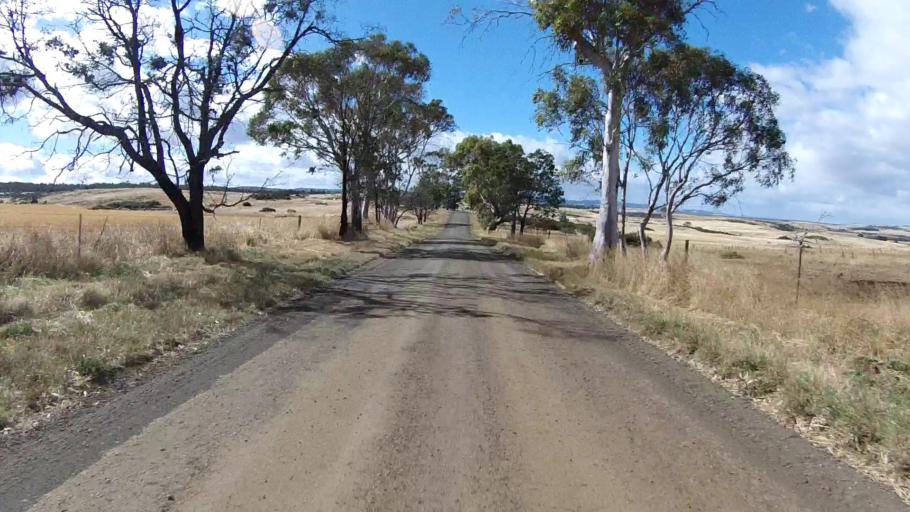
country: AU
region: Tasmania
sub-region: Northern Midlands
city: Evandale
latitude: -41.7182
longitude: 147.4223
